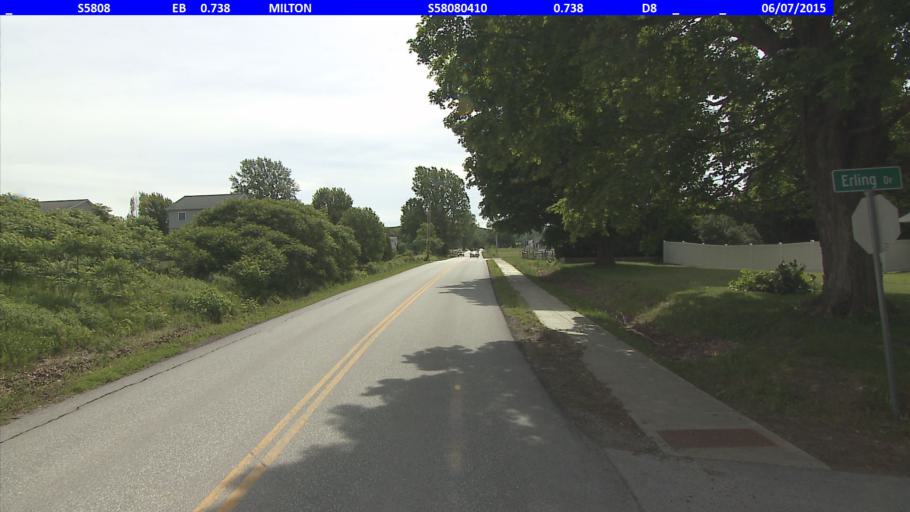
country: US
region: Vermont
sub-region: Chittenden County
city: Milton
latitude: 44.6385
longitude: -73.0989
